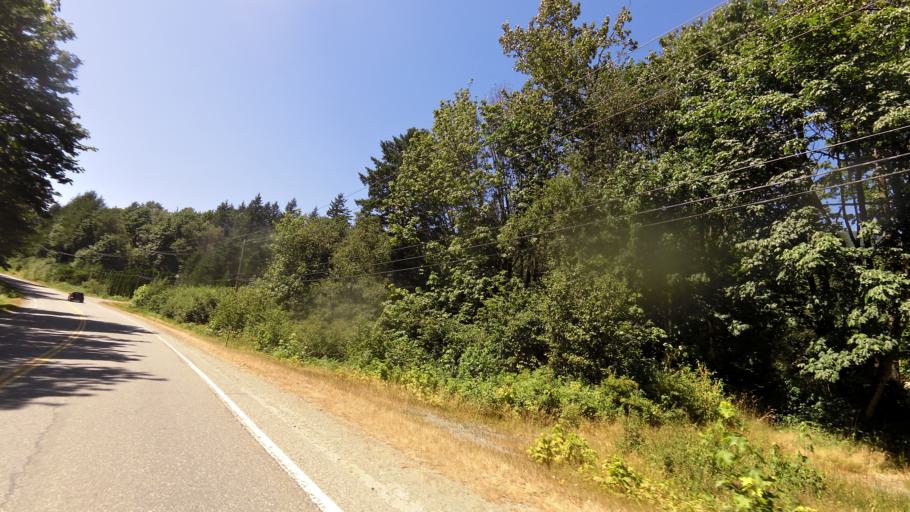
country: CA
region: British Columbia
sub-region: Fraser Valley Regional District
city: Chilliwack
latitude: 49.2030
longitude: -122.0348
